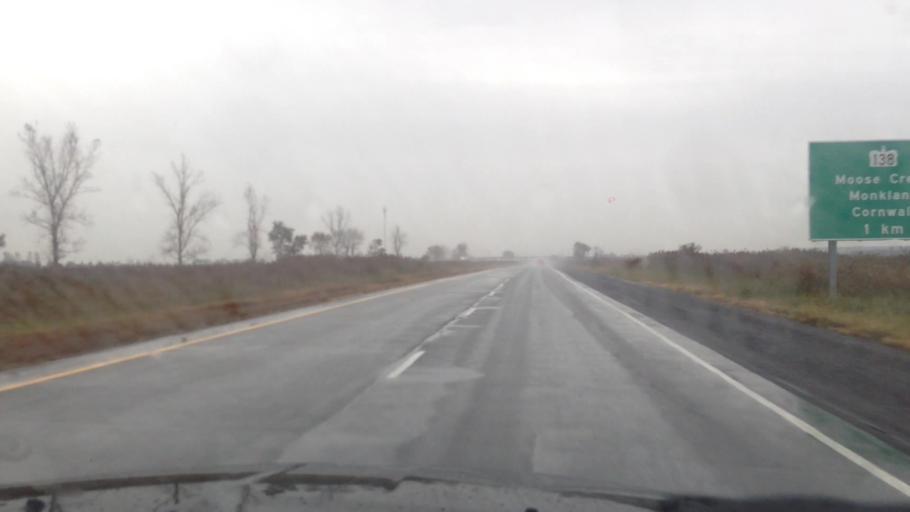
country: CA
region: Ontario
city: Casselman
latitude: 45.3231
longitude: -75.0015
